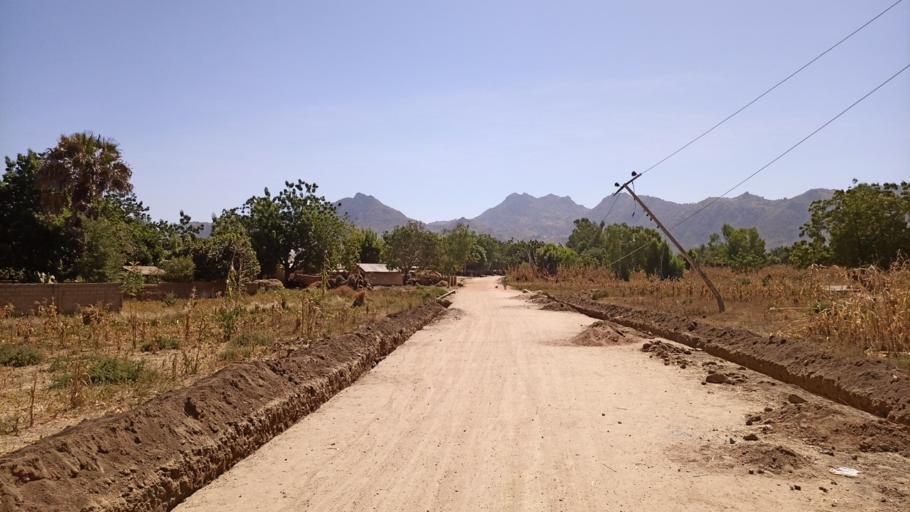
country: NG
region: Adamawa
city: Madagali
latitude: 10.7963
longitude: 13.5735
